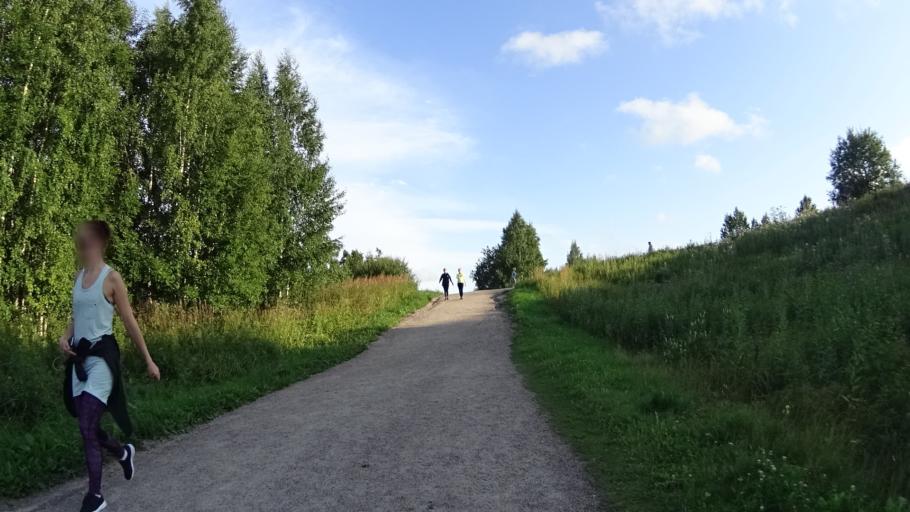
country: FI
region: Uusimaa
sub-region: Helsinki
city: Teekkarikylae
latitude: 60.2496
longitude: 24.8472
